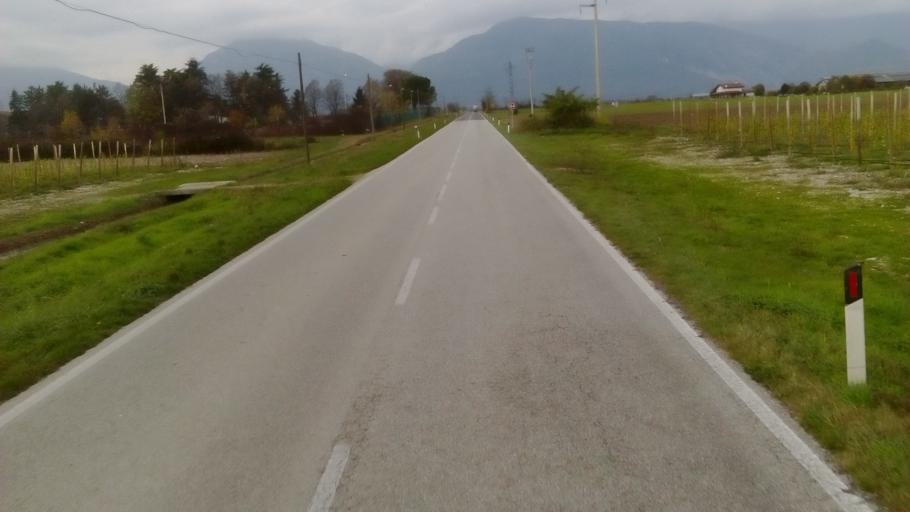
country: IT
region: Friuli Venezia Giulia
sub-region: Provincia di Pordenone
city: Vajont
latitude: 46.1179
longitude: 12.7338
